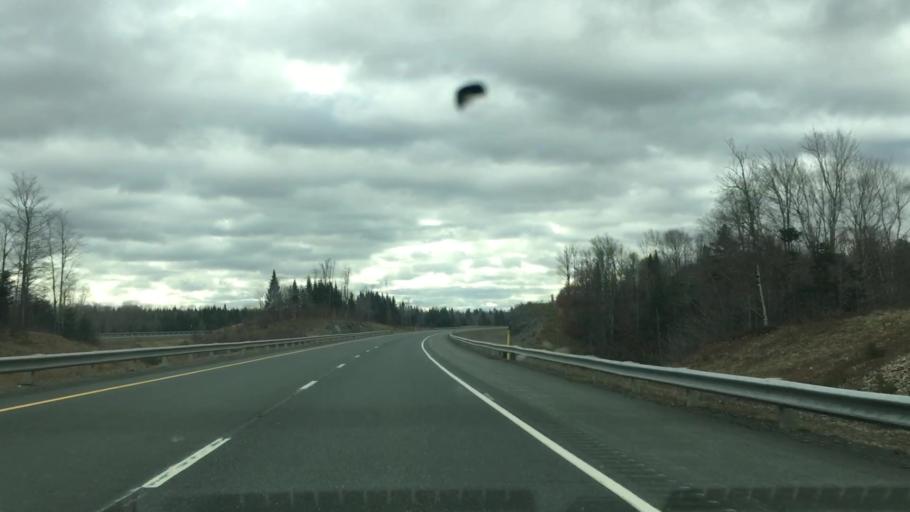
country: US
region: Maine
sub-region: Aroostook County
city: Easton
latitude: 46.6227
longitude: -67.7389
